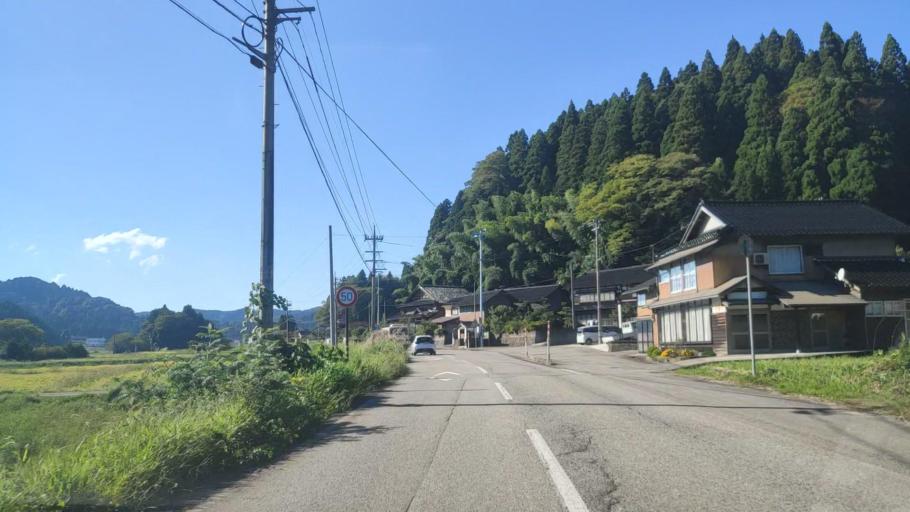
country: JP
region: Ishikawa
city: Nanao
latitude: 37.2779
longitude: 137.0520
